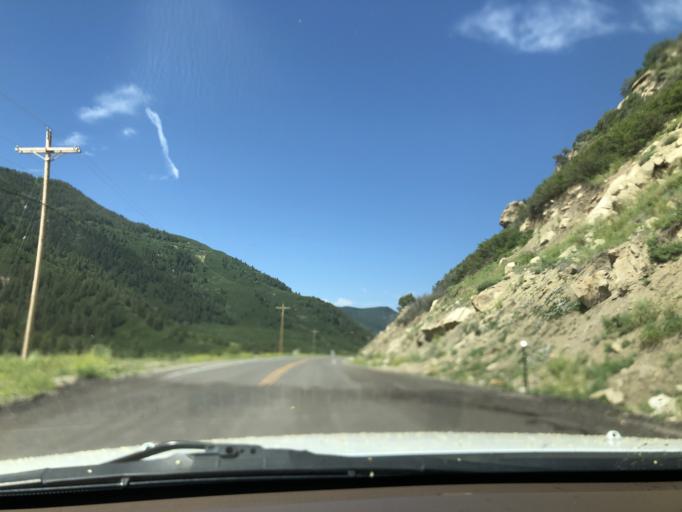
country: US
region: Colorado
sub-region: Delta County
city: Paonia
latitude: 38.9348
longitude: -107.3958
